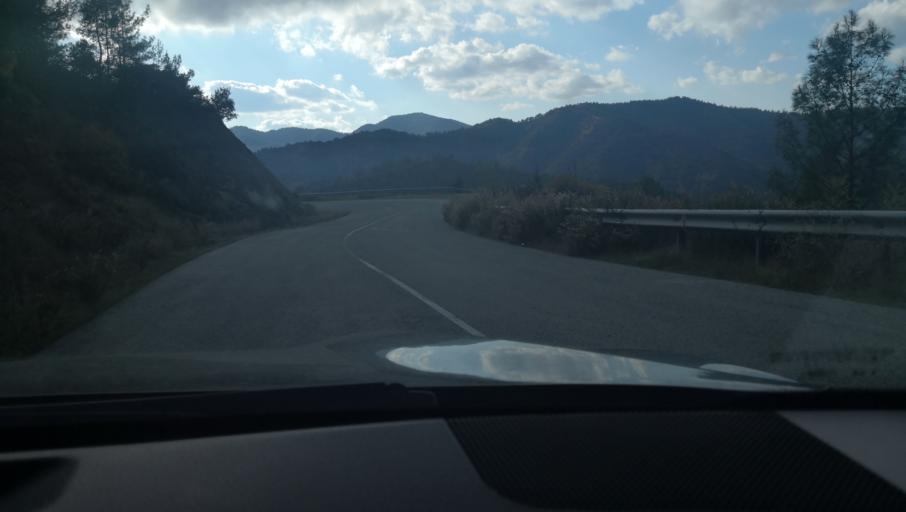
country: CY
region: Lefkosia
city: Lefka
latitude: 35.0582
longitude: 32.7492
